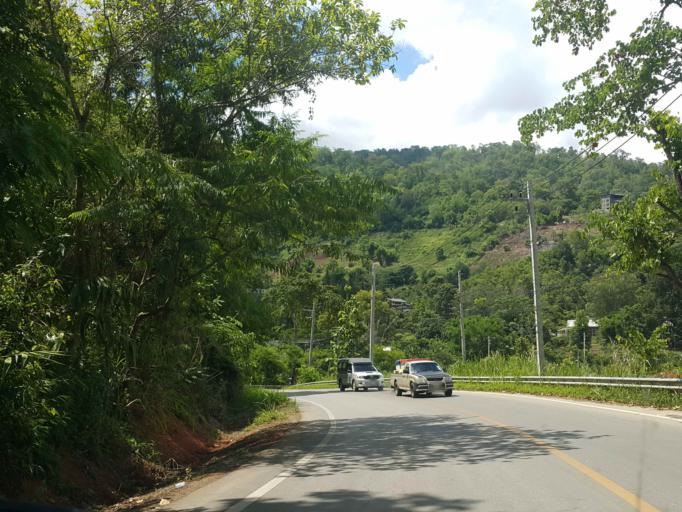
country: TH
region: Chiang Mai
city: Samoeng
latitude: 18.8826
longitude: 98.8144
